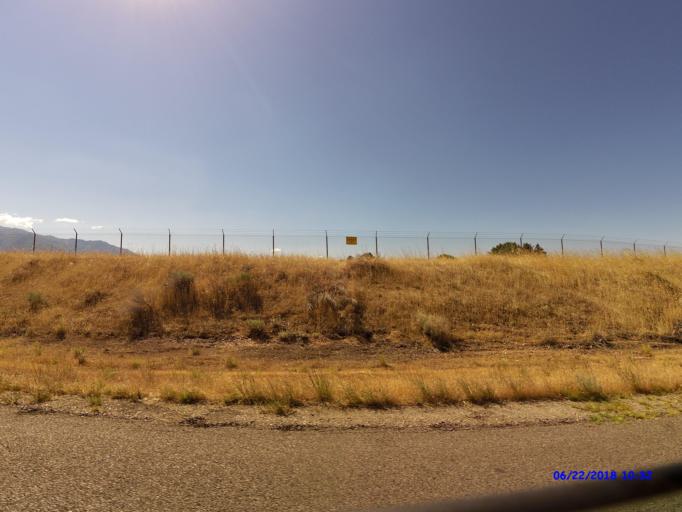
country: US
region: Utah
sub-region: Weber County
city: West Haven
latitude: 41.1981
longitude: -112.0249
